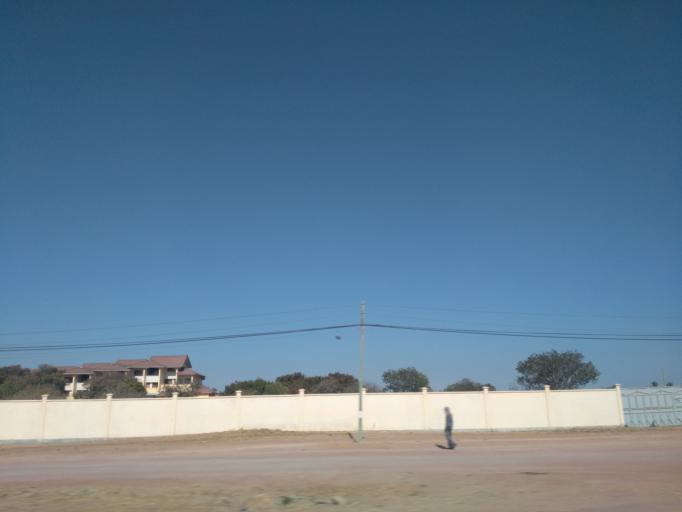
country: TZ
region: Dodoma
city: Dodoma
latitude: -6.1261
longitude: 35.7464
